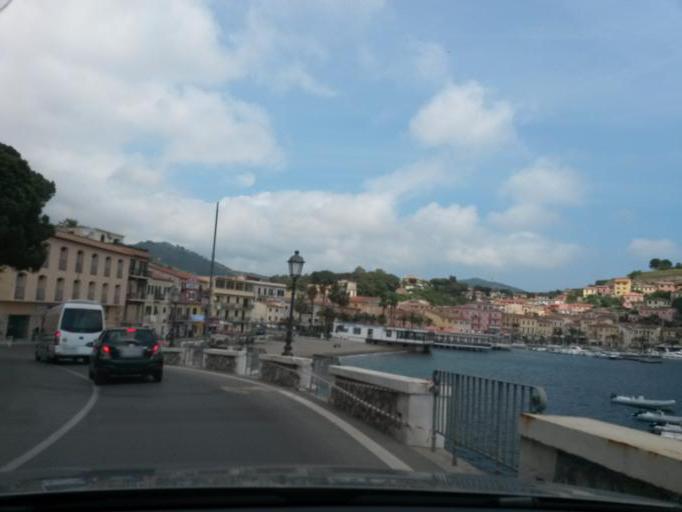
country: IT
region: Tuscany
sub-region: Provincia di Livorno
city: Porto Azzurro
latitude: 42.7636
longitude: 10.3950
